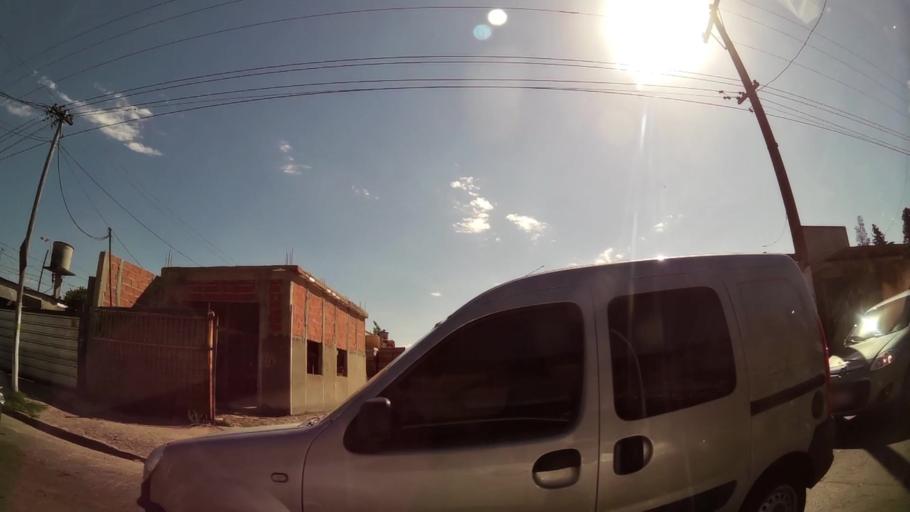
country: AR
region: Buenos Aires
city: Santa Catalina - Dique Lujan
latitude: -34.4879
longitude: -58.6944
